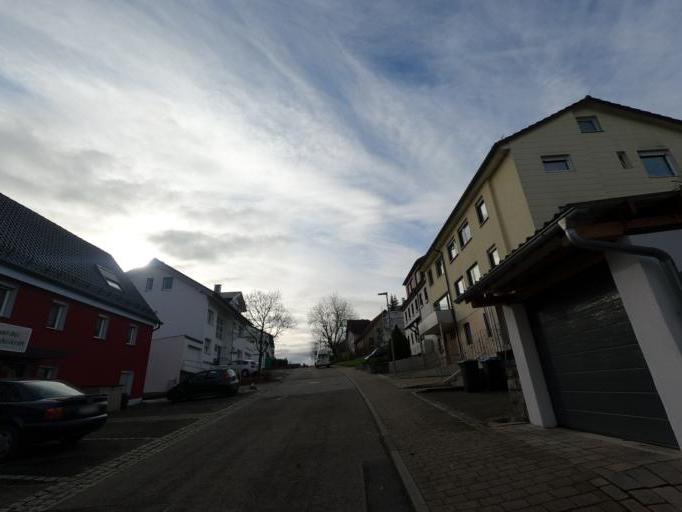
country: DE
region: Baden-Wuerttemberg
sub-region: Regierungsbezirk Stuttgart
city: Albershausen
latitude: 48.6900
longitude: 9.5621
